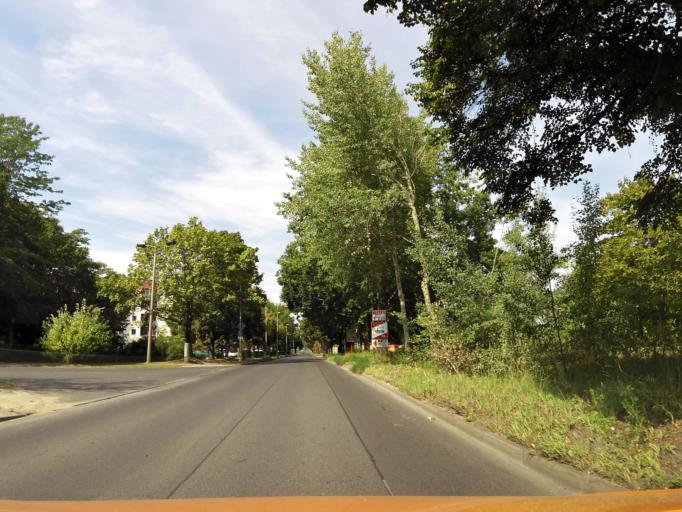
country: DE
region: Brandenburg
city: Stahnsdorf
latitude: 52.3841
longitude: 13.2415
